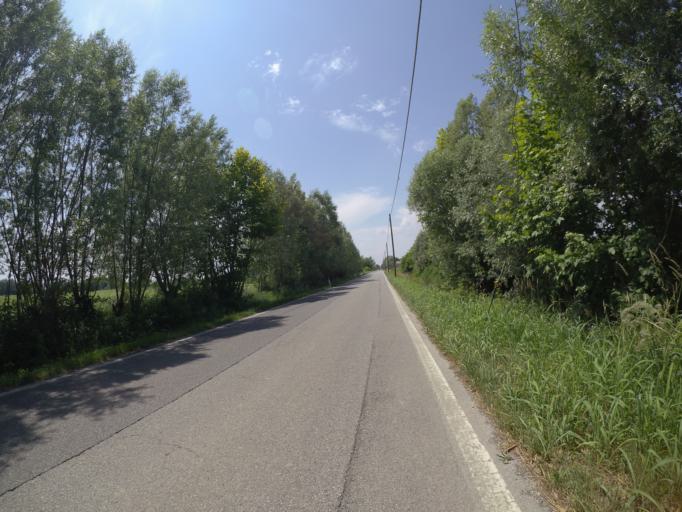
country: IT
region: Friuli Venezia Giulia
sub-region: Provincia di Udine
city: Teor
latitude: 45.8714
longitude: 13.0660
